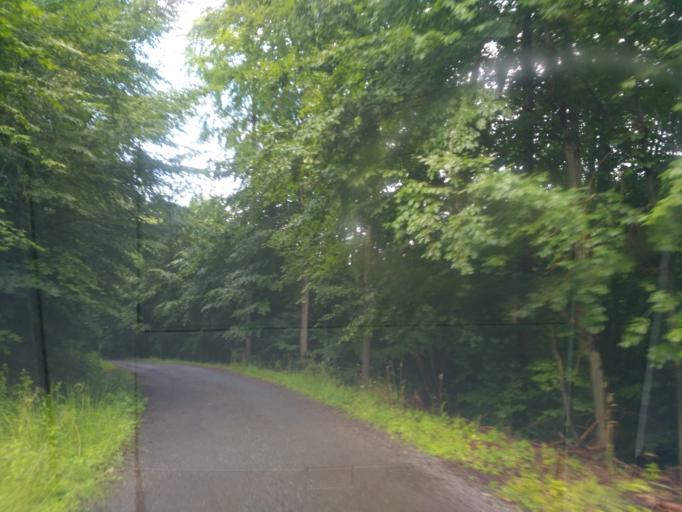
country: SK
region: Kosicky
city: Secovce
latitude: 48.5974
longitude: 21.5097
